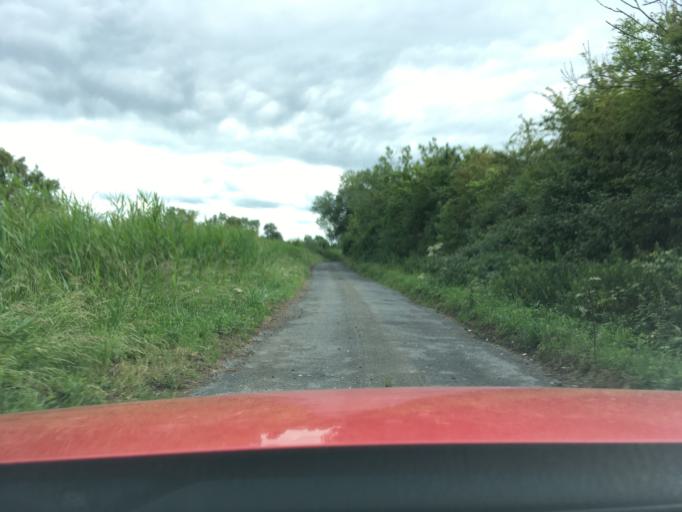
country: GB
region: England
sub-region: Gloucestershire
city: Cinderford
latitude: 51.8043
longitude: -2.4209
